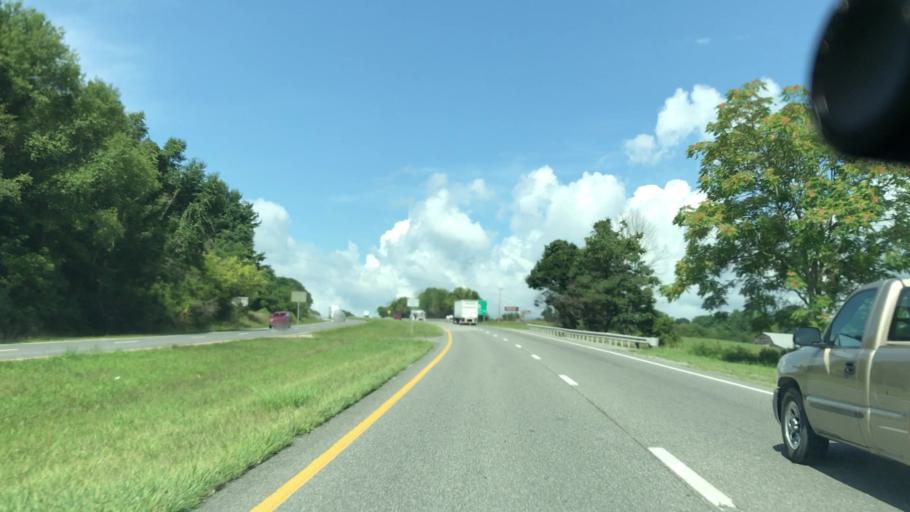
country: US
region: Virginia
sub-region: Giles County
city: Pembroke
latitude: 37.3320
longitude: -80.6839
